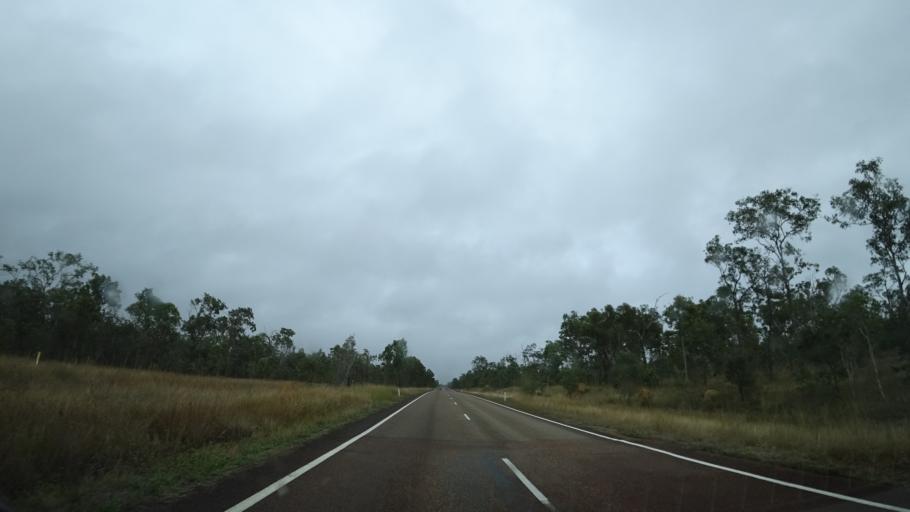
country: AU
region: Queensland
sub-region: Tablelands
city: Ravenshoe
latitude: -17.6857
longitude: 145.2299
